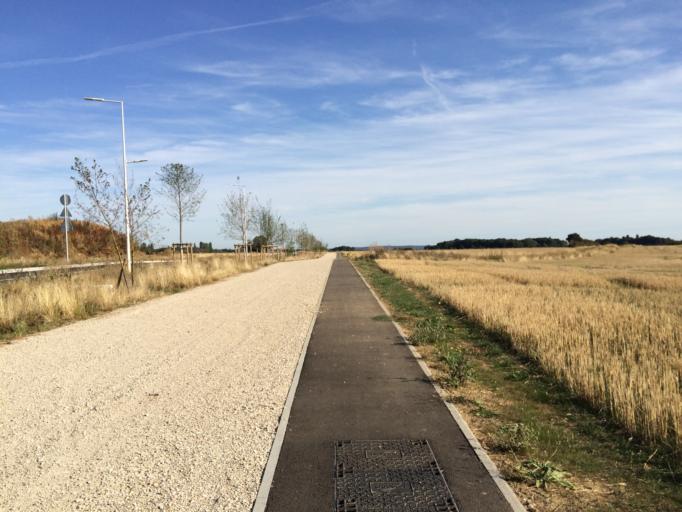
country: FR
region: Ile-de-France
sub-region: Departement de l'Essonne
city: Bretigny-sur-Orge
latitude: 48.5940
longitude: 2.3128
